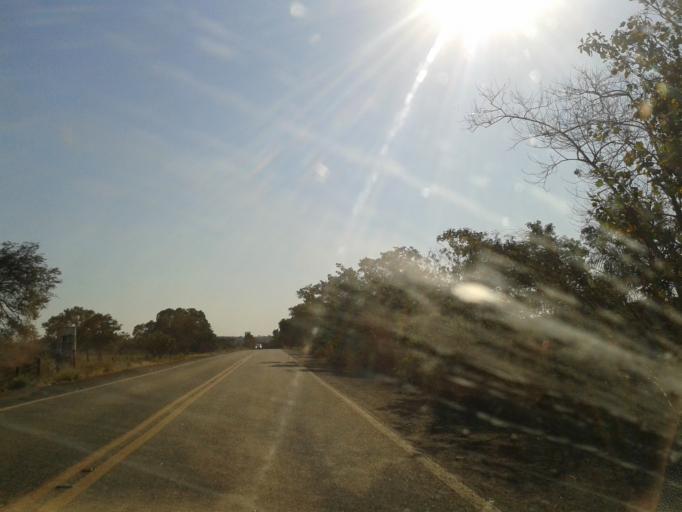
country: BR
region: Goias
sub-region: Mozarlandia
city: Mozarlandia
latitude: -14.9907
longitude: -50.5848
